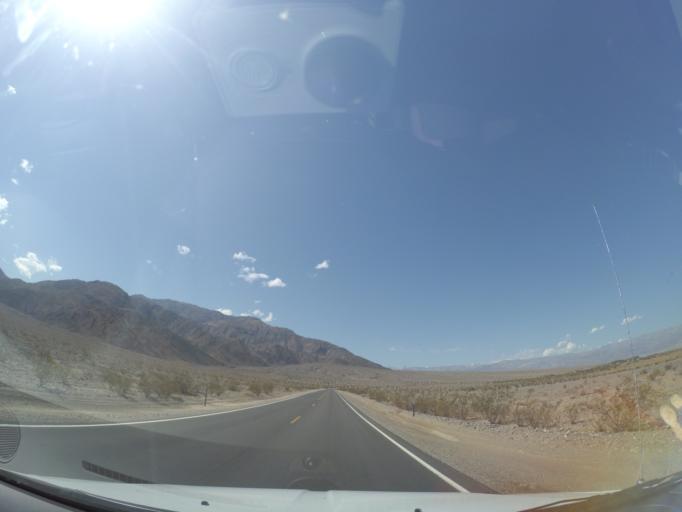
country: US
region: Nevada
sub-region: Nye County
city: Beatty
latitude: 36.6087
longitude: -117.0915
